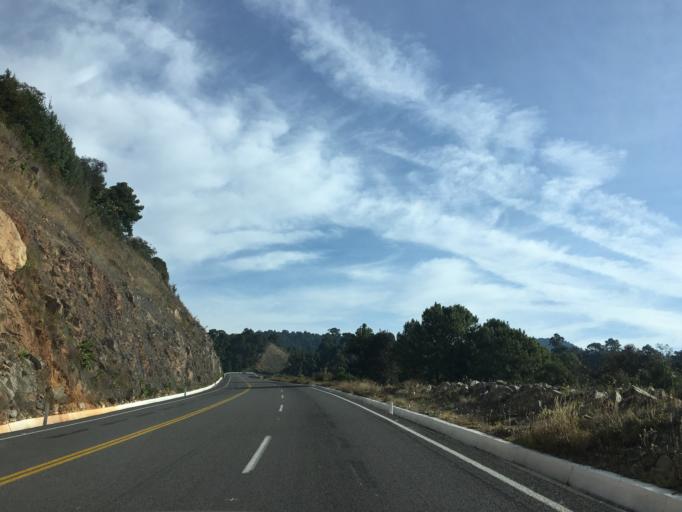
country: MX
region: Mexico
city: San Bartolo
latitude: 19.2668
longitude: -100.0631
